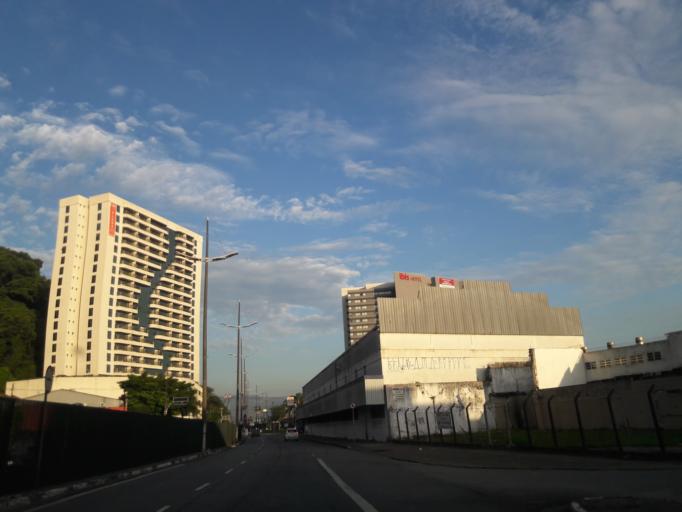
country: BR
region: Sao Paulo
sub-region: Santos
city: Santos
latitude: -23.9331
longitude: -46.3365
